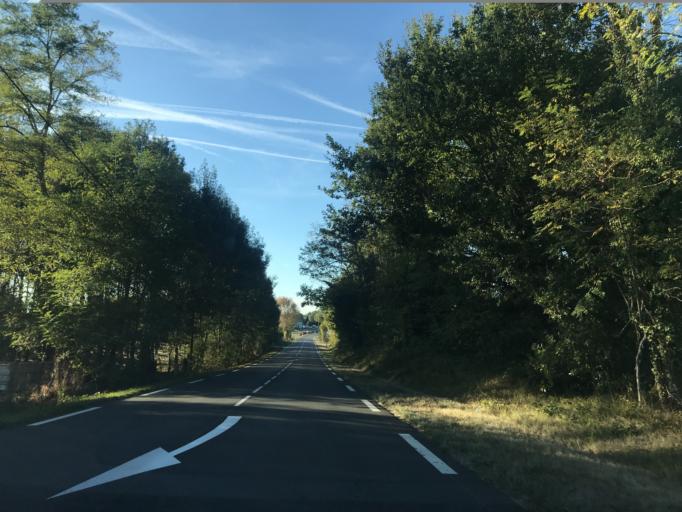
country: FR
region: Poitou-Charentes
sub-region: Departement de la Charente-Maritime
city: Montguyon
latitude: 45.1856
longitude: -0.1320
